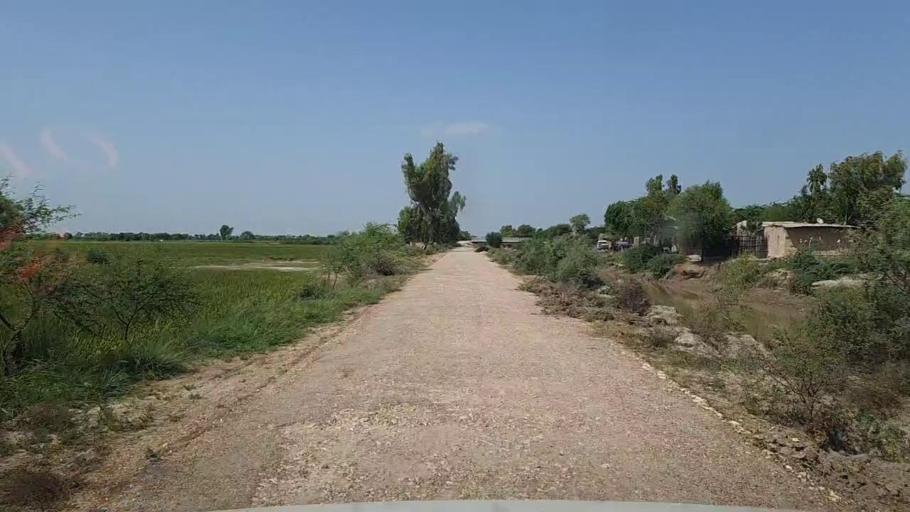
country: PK
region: Sindh
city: Kario
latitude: 24.6601
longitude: 68.5488
